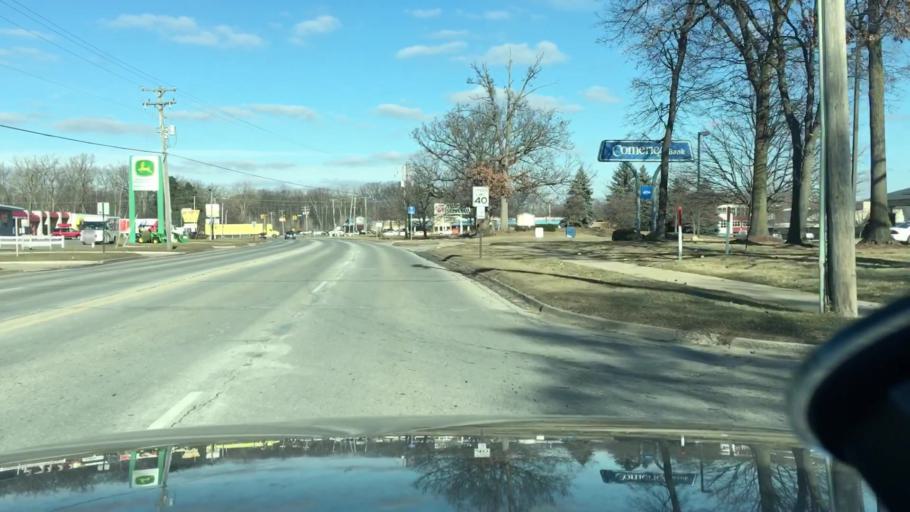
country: US
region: Michigan
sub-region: Jackson County
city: Jackson
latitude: 42.2741
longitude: -84.4529
